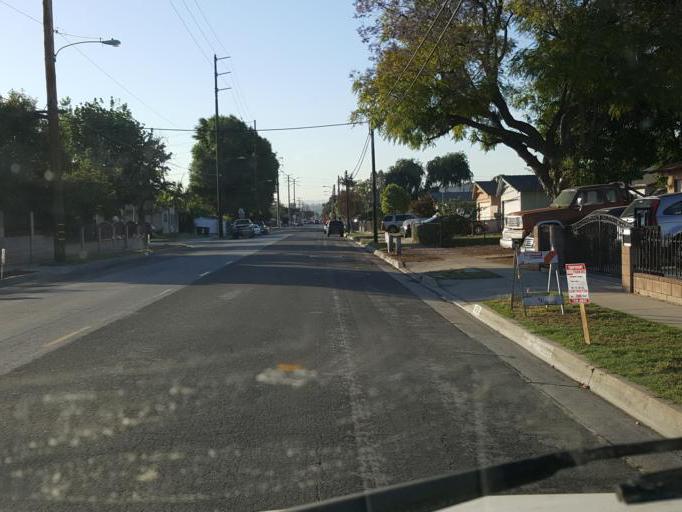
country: US
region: California
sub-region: Los Angeles County
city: West Puente Valley
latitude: 34.0481
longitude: -117.9577
